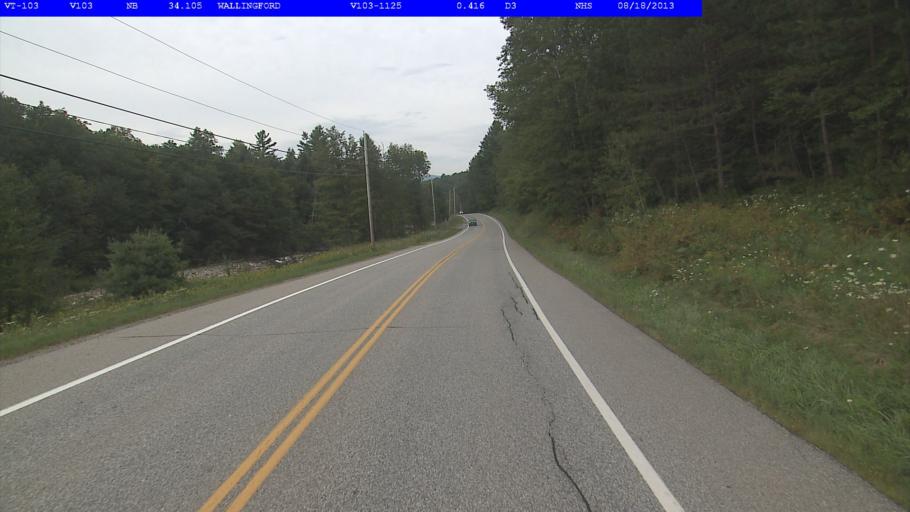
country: US
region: Vermont
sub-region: Rutland County
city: Rutland
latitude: 43.4527
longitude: -72.8783
